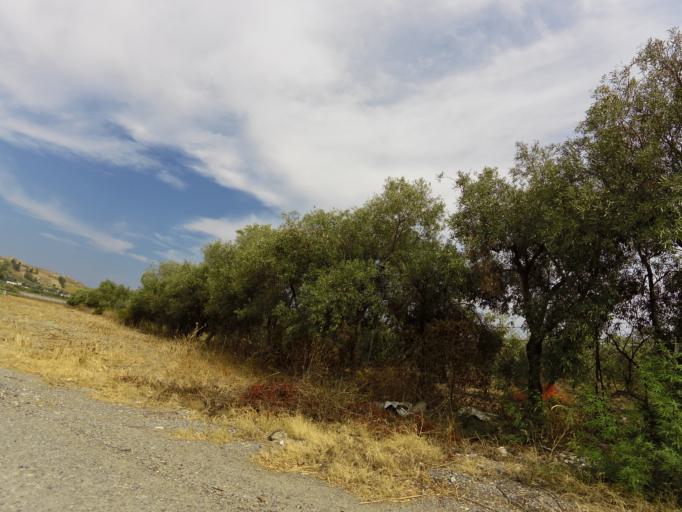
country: IT
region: Calabria
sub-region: Provincia di Reggio Calabria
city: Monasterace
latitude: 38.4483
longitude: 16.5212
